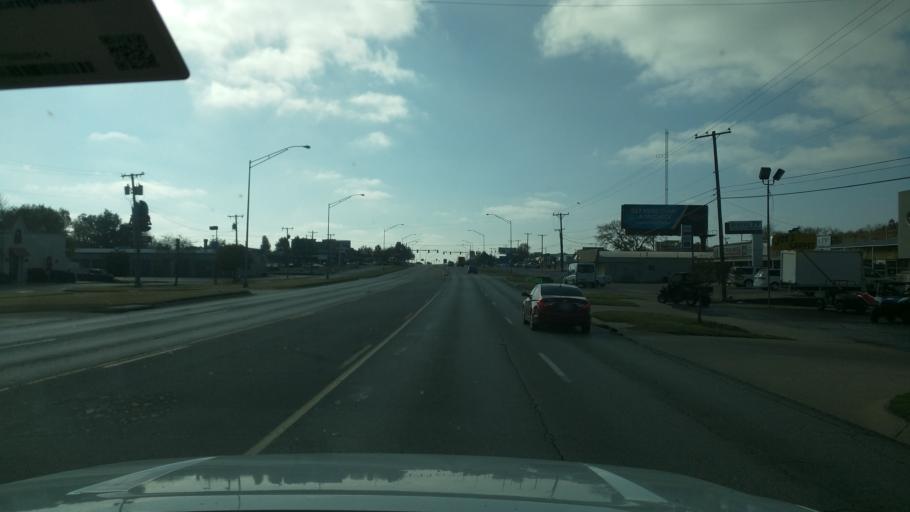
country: US
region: Oklahoma
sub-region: Washington County
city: Dewey
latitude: 36.7598
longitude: -95.9356
